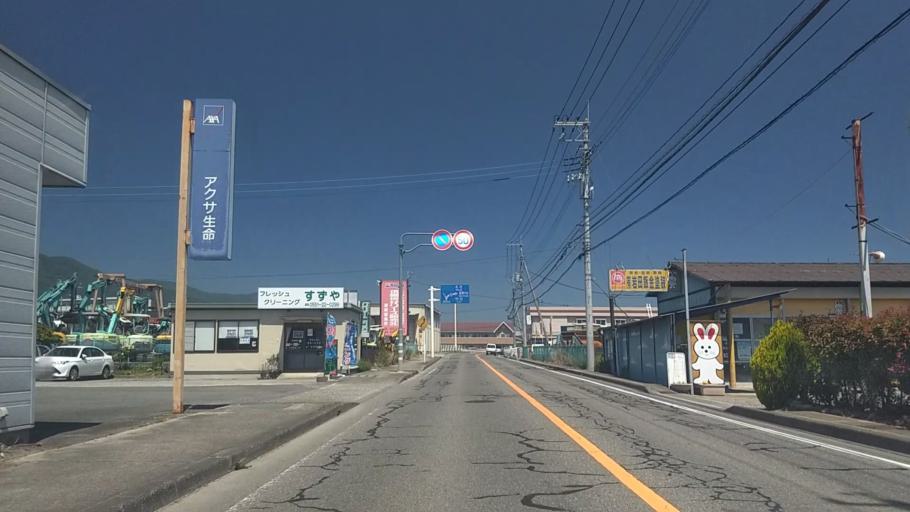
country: JP
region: Yamanashi
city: Nirasaki
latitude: 35.6946
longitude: 138.4575
